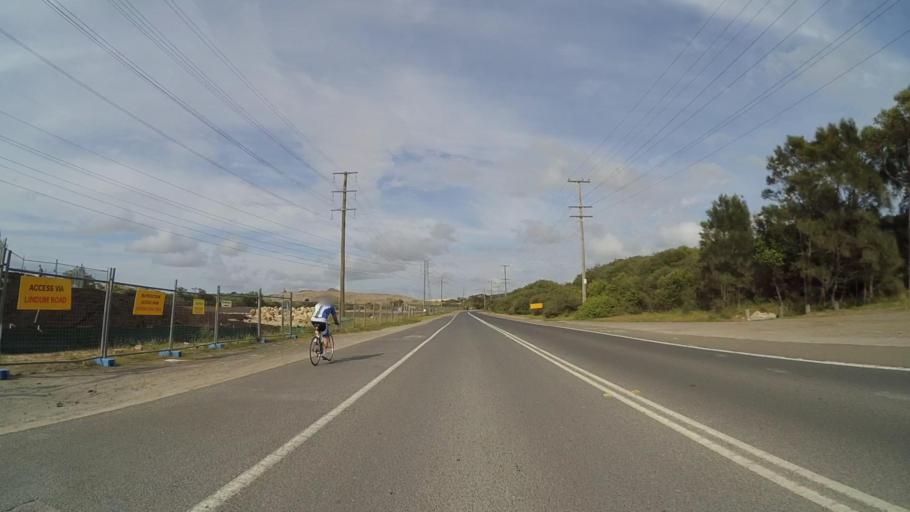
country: AU
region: New South Wales
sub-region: Sutherland Shire
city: Kurnell
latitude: -34.0251
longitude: 151.1828
